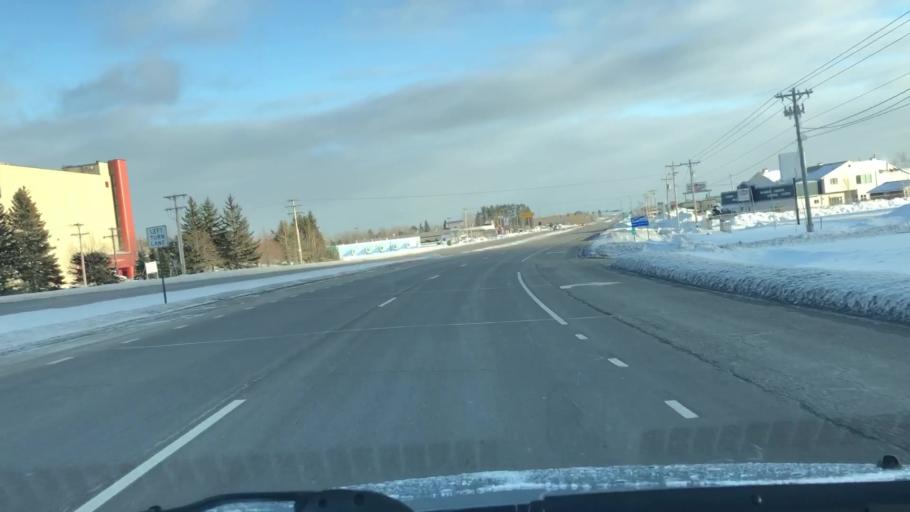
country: US
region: Minnesota
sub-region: Saint Louis County
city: Hermantown
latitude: 46.8361
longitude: -92.2098
